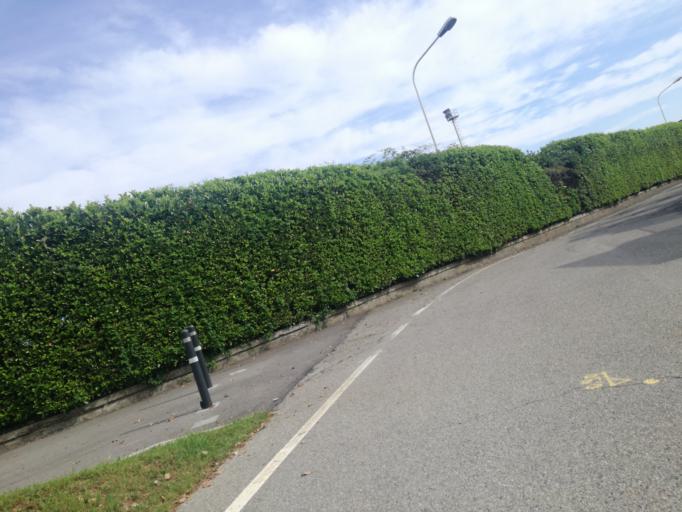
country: IT
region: Lombardy
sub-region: Provincia di Bergamo
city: Calusco d'Adda
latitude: 45.6876
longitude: 9.4612
